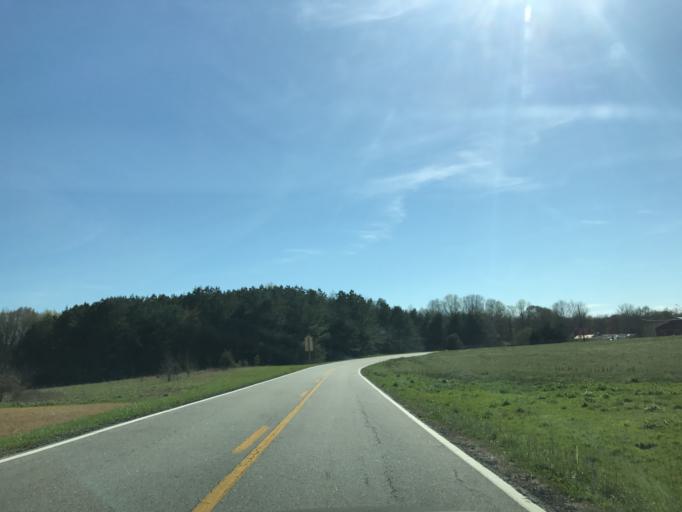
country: US
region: Maryland
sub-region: Caroline County
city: Ridgely
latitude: 38.9773
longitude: -75.9564
